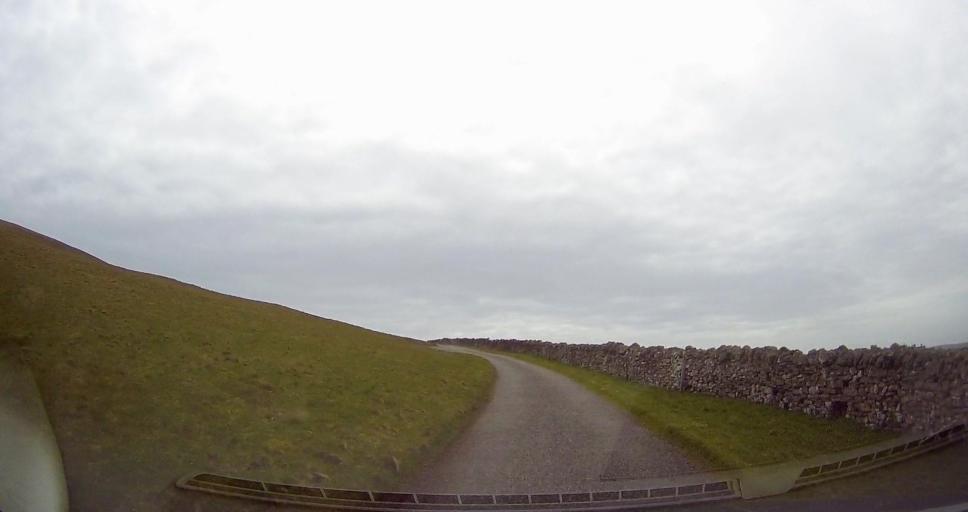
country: GB
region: Scotland
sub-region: Shetland Islands
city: Sandwick
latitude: 59.8714
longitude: -1.2774
